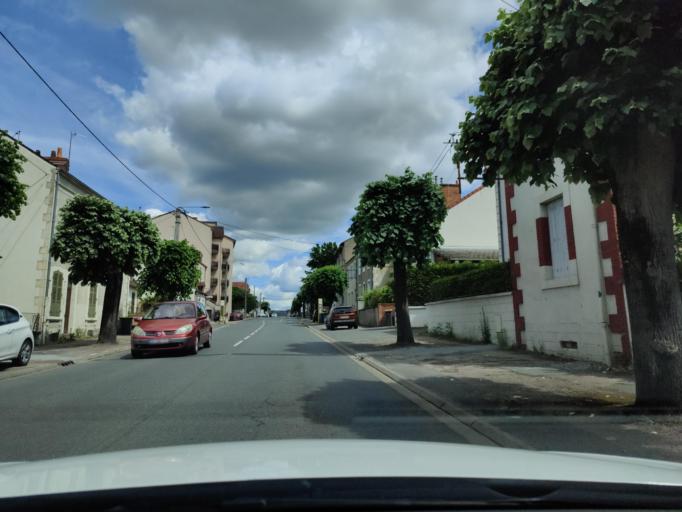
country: FR
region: Auvergne
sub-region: Departement de l'Allier
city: Montlucon
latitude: 46.3316
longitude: 2.6089
